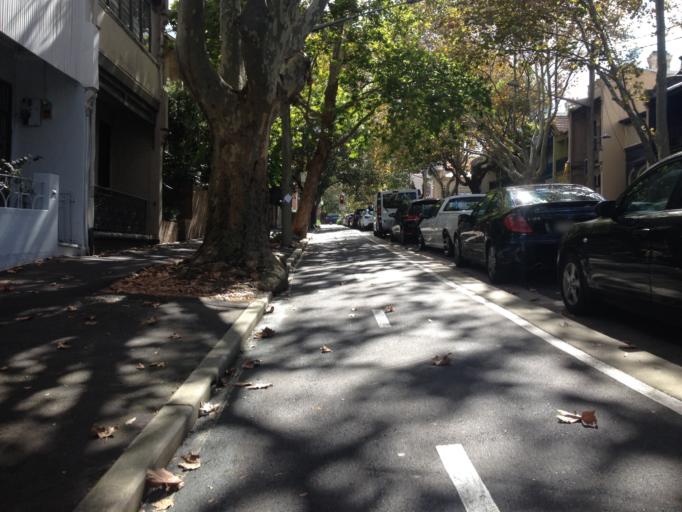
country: AU
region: New South Wales
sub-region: City of Sydney
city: Darlinghurst
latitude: -33.8850
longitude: 151.2158
